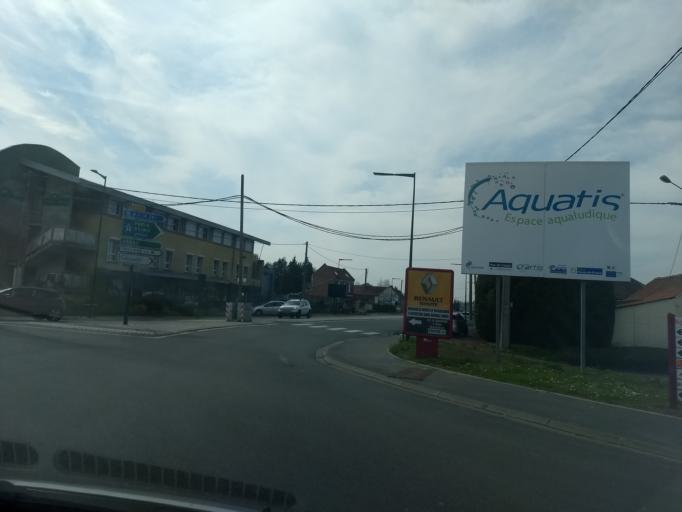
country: FR
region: Nord-Pas-de-Calais
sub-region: Departement du Pas-de-Calais
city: Vitry-en-Artois
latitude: 50.3334
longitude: 2.9852
